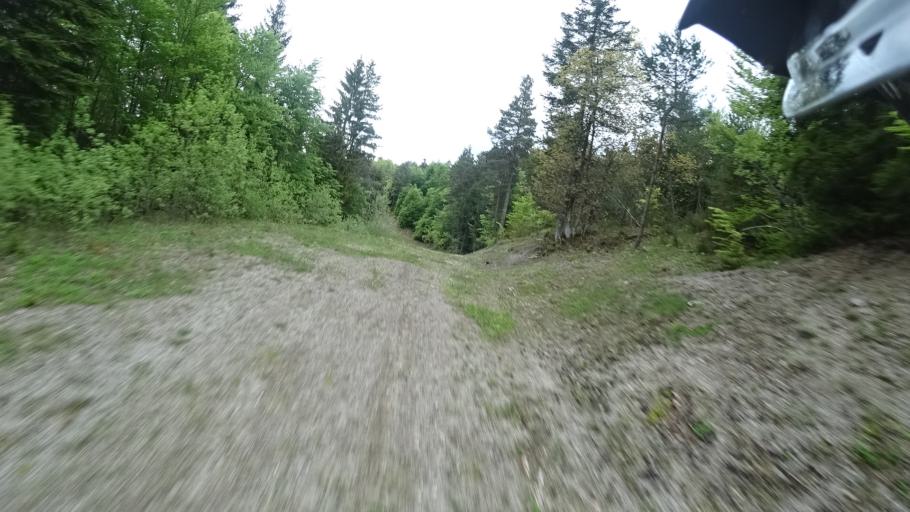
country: HR
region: Licko-Senjska
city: Jezerce
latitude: 44.8804
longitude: 15.4323
